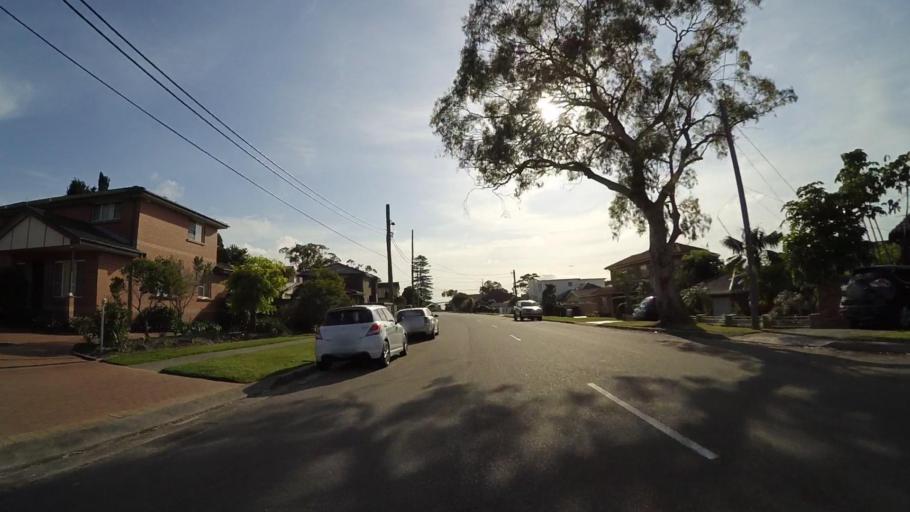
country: AU
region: New South Wales
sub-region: Kogarah
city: Blakehurst
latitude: -34.0117
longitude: 151.1121
